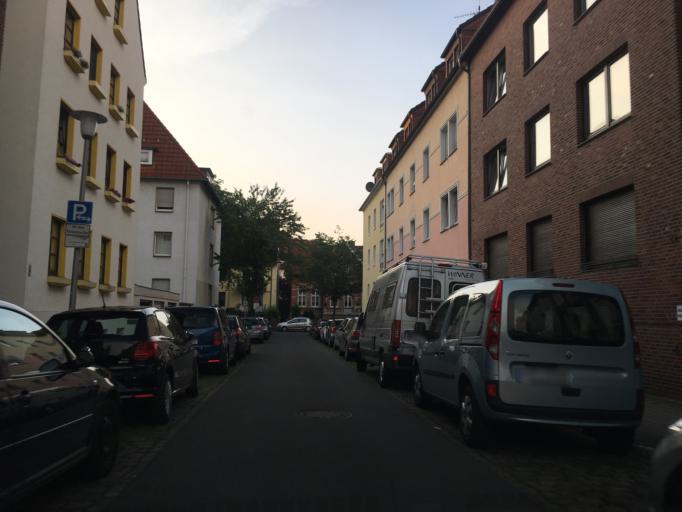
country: DE
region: North Rhine-Westphalia
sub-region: Regierungsbezirk Munster
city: Muenster
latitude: 51.9637
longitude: 7.6436
